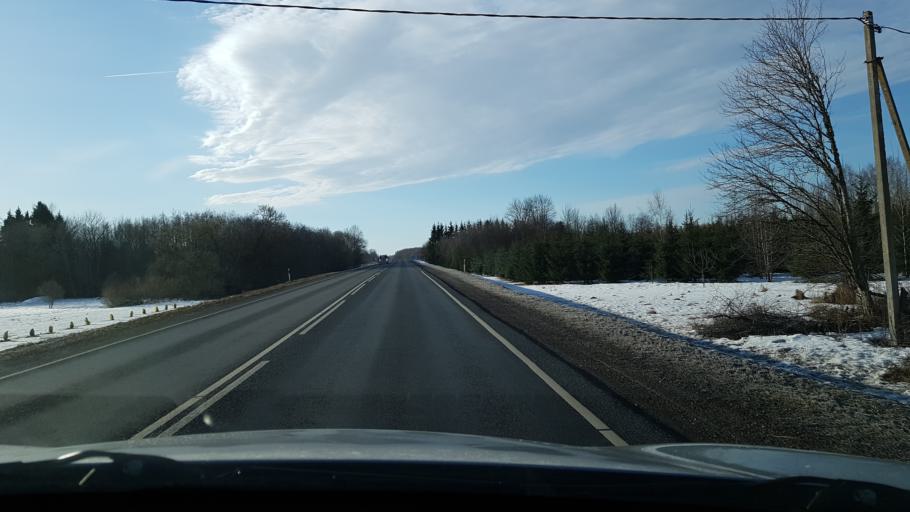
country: EE
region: Viljandimaa
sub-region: Vohma linn
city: Vohma
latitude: 58.6394
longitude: 25.5761
